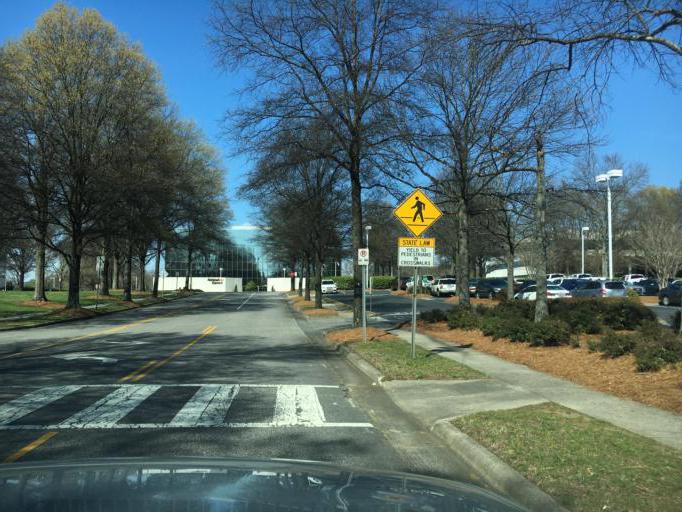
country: US
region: North Carolina
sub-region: Mecklenburg County
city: Charlotte
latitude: 35.1573
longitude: -80.8341
